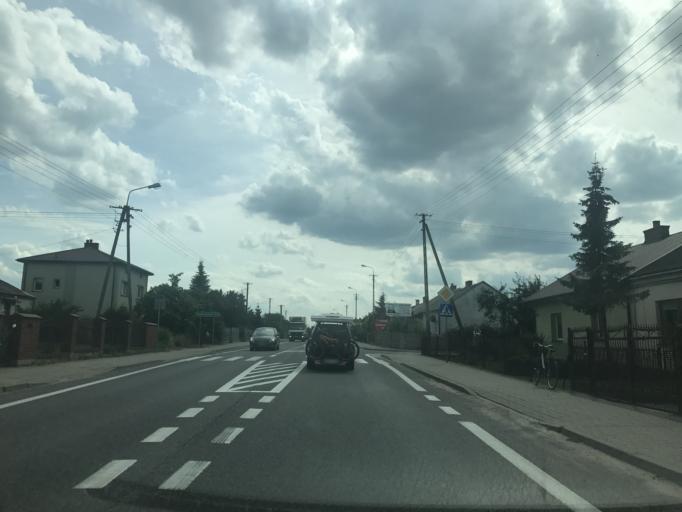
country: PL
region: Masovian Voivodeship
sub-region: Powiat mlawski
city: Wisniewo
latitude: 53.0657
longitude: 20.3485
